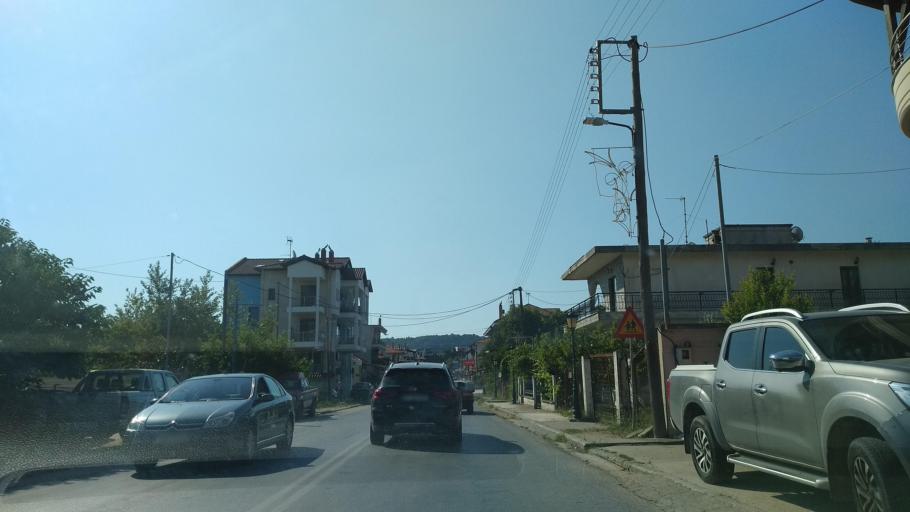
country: GR
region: Central Macedonia
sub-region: Nomos Chalkidikis
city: Ierissos
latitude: 40.4000
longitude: 23.8712
